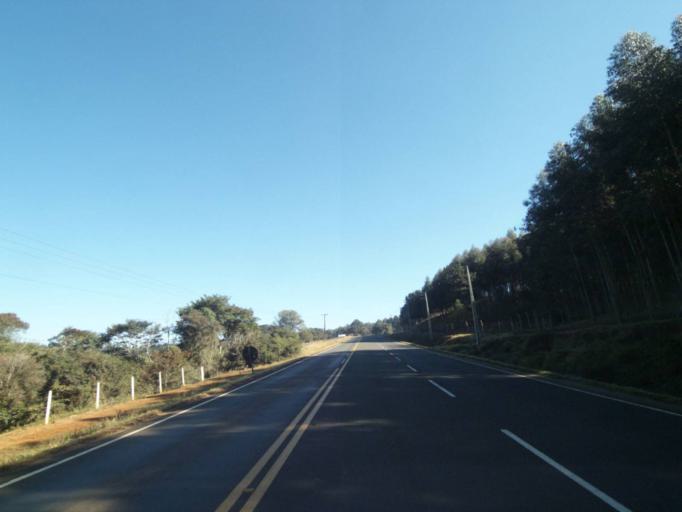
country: BR
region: Parana
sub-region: Tibagi
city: Tibagi
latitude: -24.5142
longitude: -50.4287
